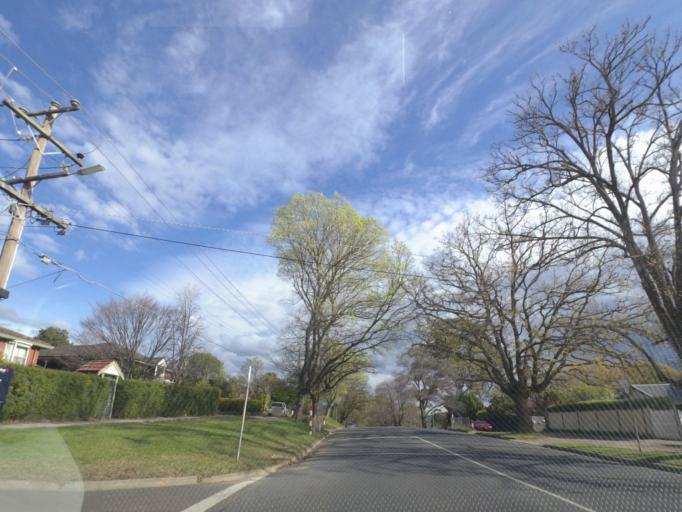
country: AU
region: Victoria
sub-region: Yarra Ranges
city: Lilydale
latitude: -37.7527
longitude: 145.3561
